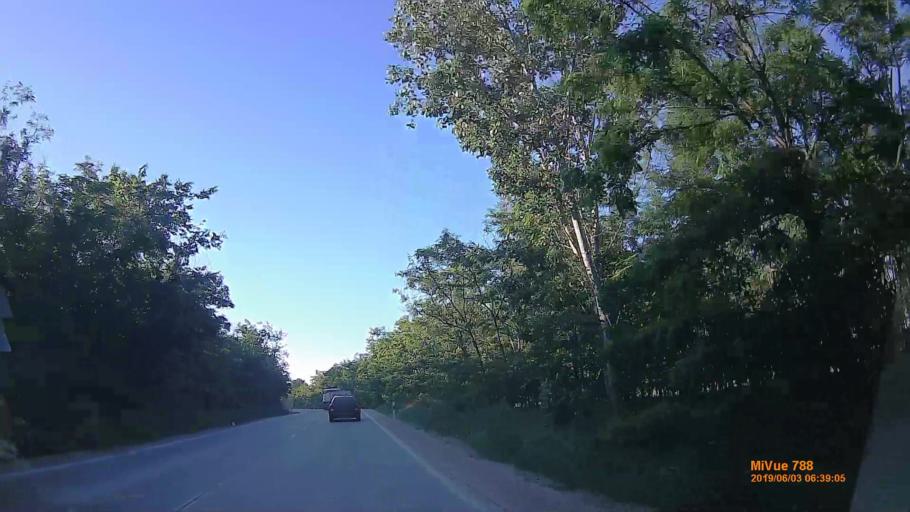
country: HU
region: Pest
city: Dunavarsany
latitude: 47.2900
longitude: 19.0970
